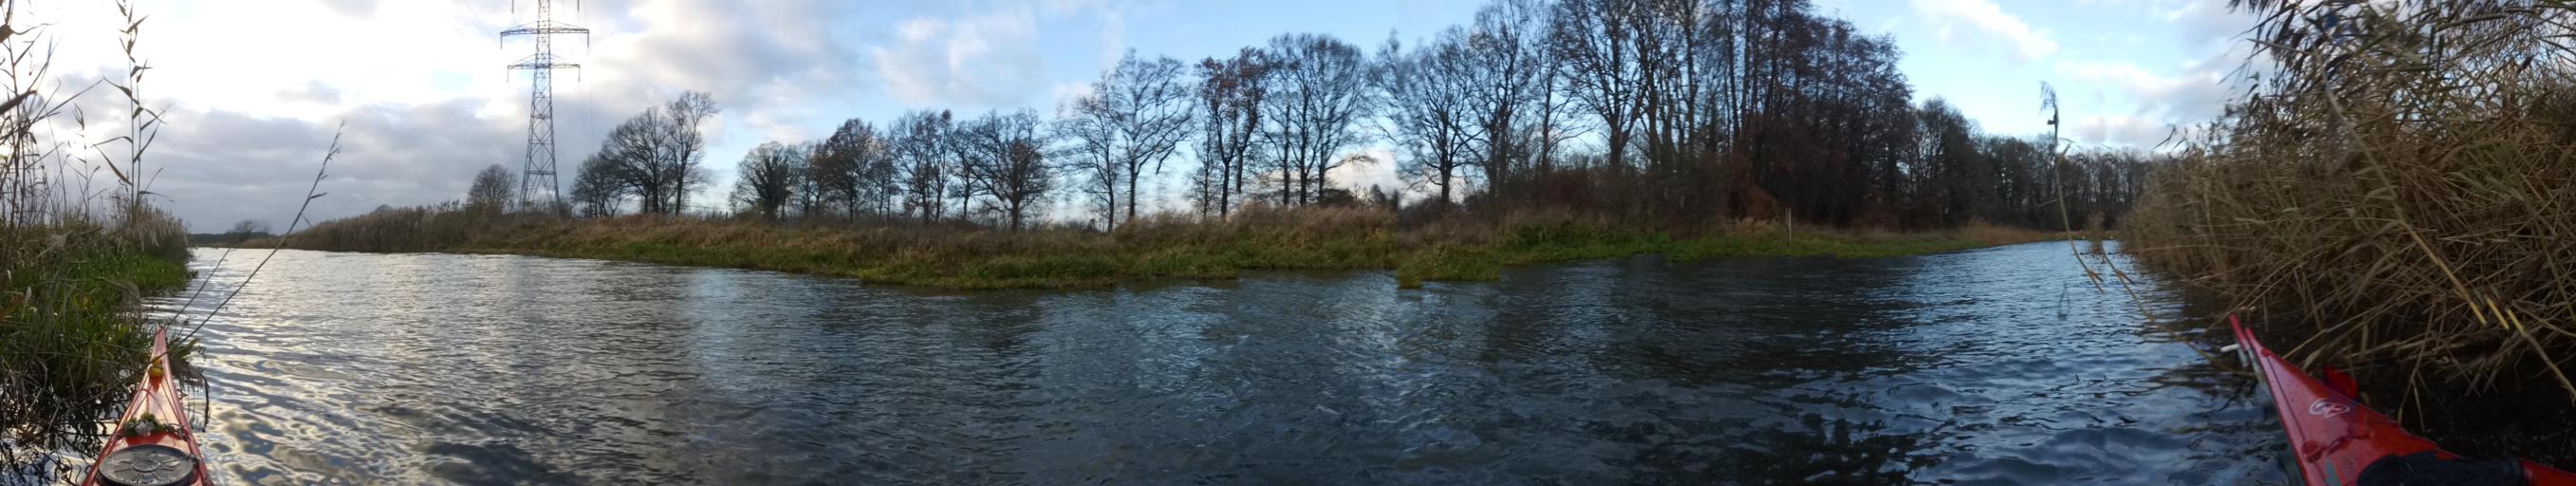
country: NL
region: Gelderland
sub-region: Gemeente Lochem
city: Laren
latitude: 52.1630
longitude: 6.3671
